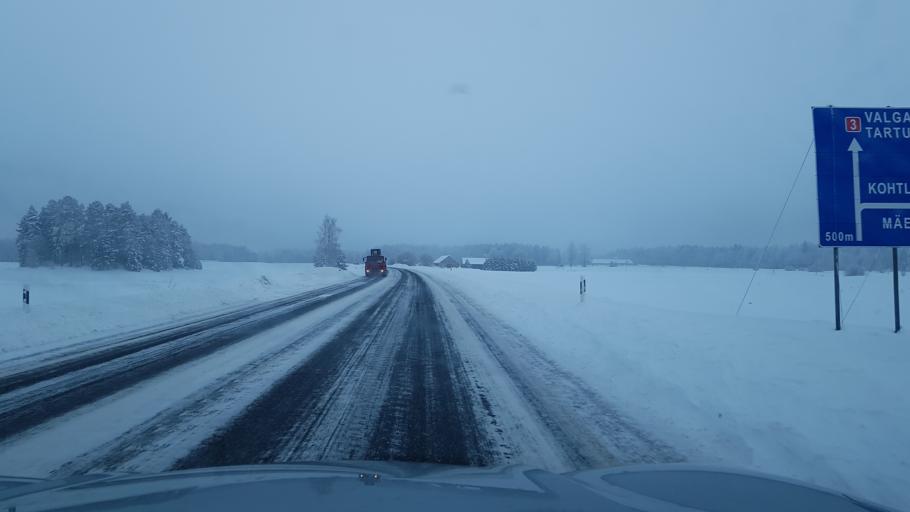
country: EE
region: Ida-Virumaa
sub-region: Johvi vald
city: Johvi
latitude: 59.2318
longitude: 27.3421
